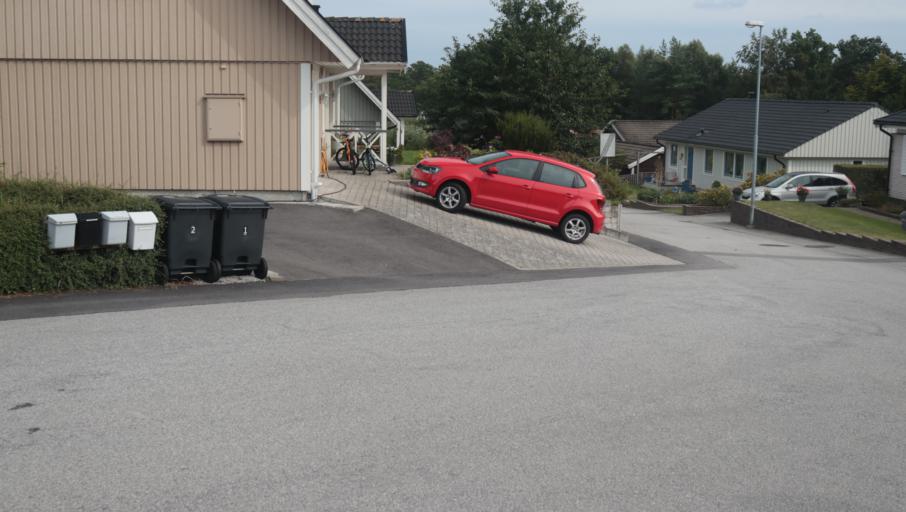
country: SE
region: Blekinge
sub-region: Karlshamns Kommun
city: Karlshamn
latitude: 56.2056
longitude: 14.8581
